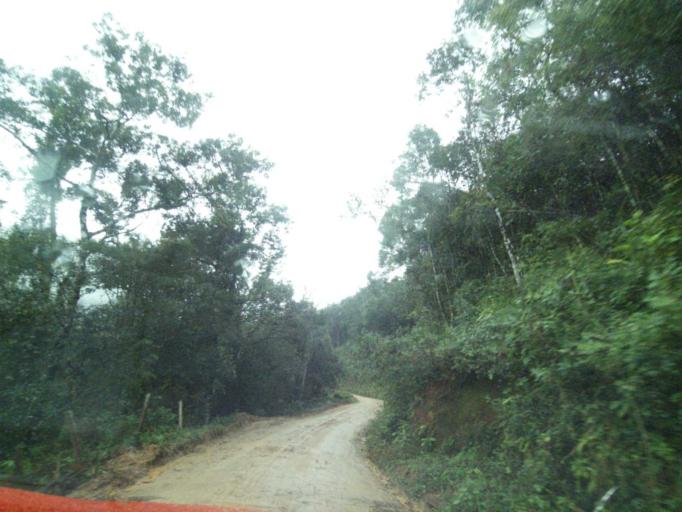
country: BR
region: Santa Catarina
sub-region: Anitapolis
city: Anitapolis
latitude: -27.9020
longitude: -49.1949
